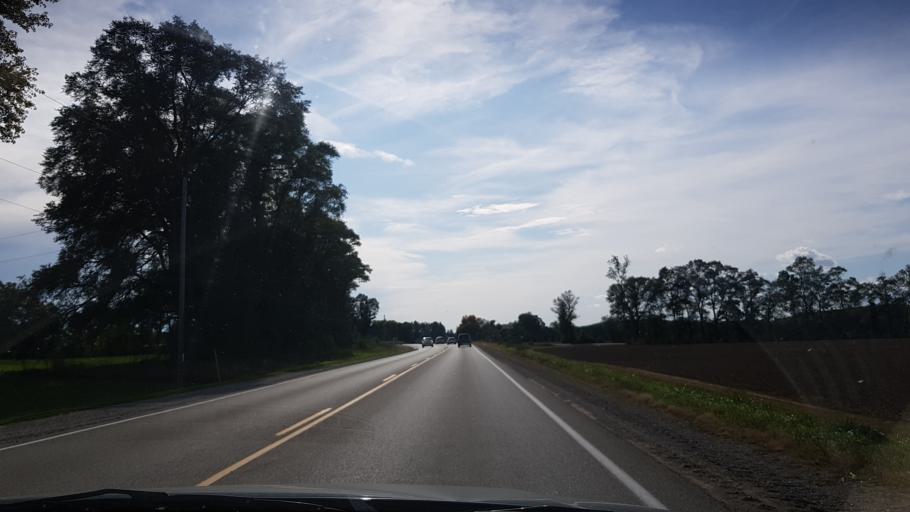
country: CA
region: Ontario
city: Delaware
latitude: 42.9307
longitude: -81.4507
